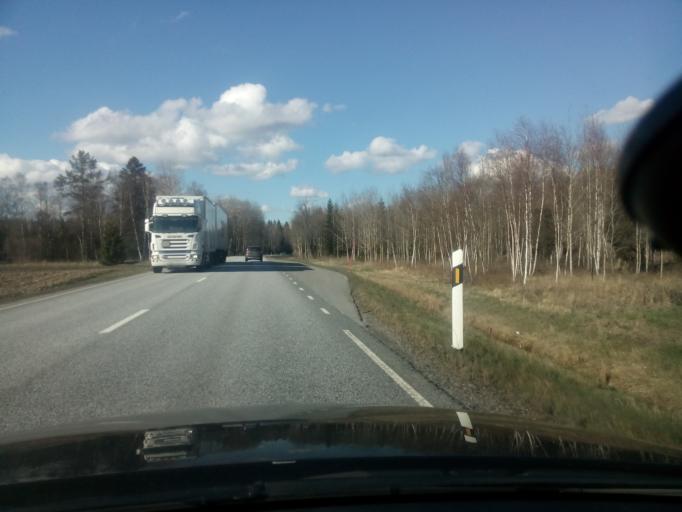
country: SE
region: Soedermanland
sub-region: Strangnas Kommun
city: Strangnas
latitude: 59.2889
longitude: 16.9773
